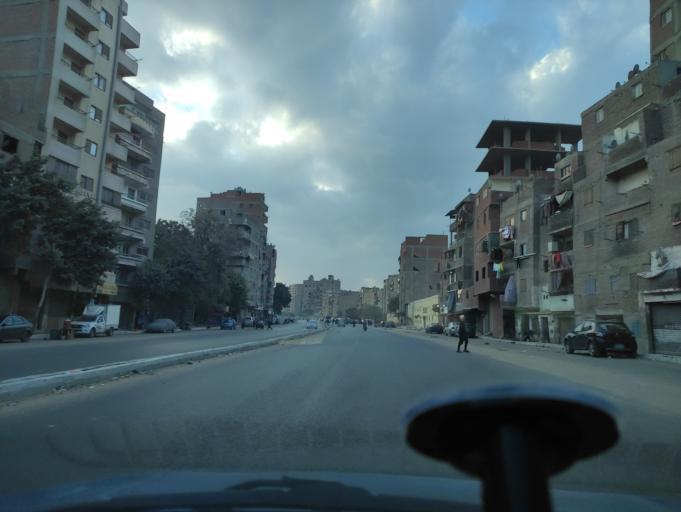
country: EG
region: Muhafazat al Qalyubiyah
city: Al Khankah
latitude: 30.1382
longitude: 31.3460
